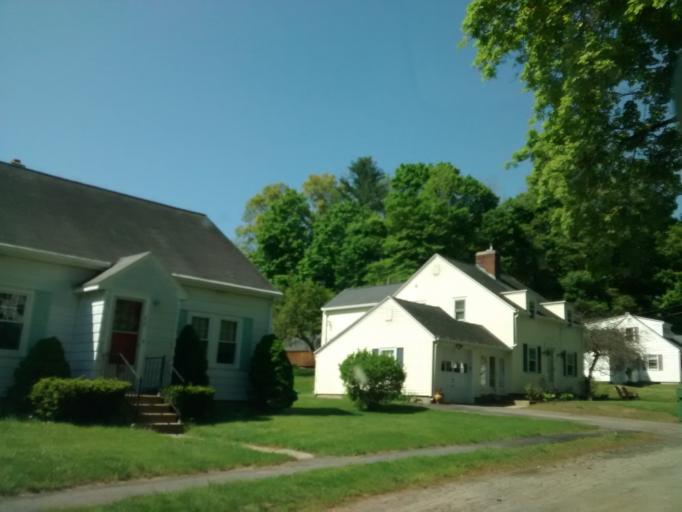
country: US
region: Massachusetts
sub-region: Worcester County
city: Whitinsville
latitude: 42.1071
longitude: -71.6650
